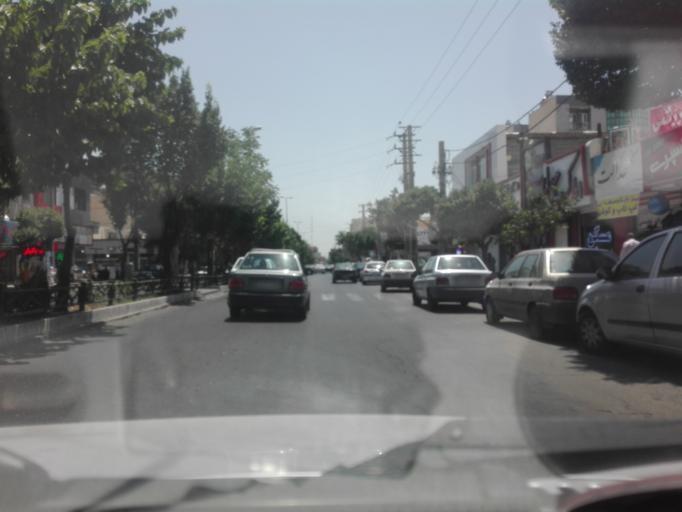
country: IR
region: Tehran
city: Shahre Jadide Andisheh
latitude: 35.7132
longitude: 50.9853
